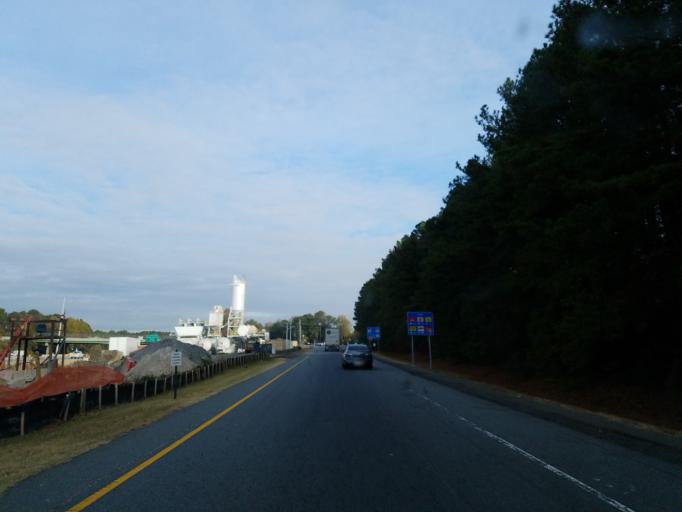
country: US
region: Georgia
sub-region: Cobb County
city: Kennesaw
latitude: 34.0310
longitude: -84.5757
